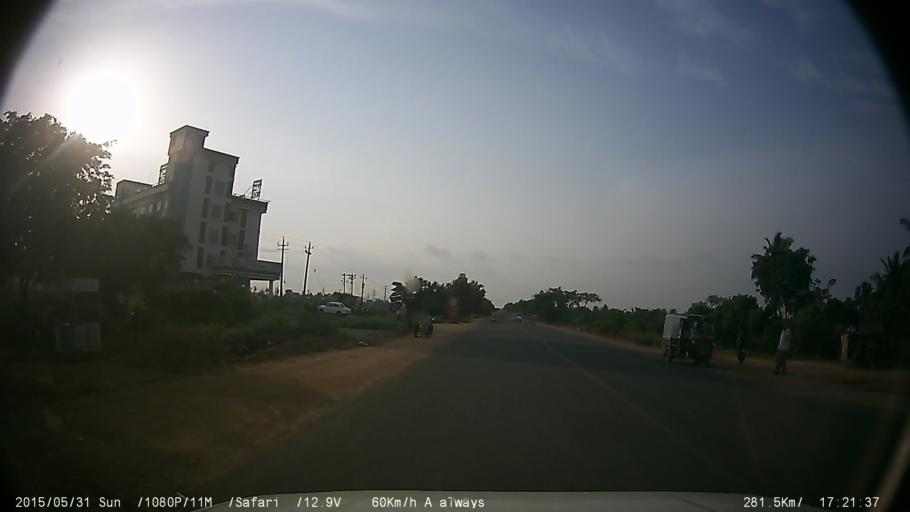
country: IN
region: Karnataka
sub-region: Chamrajnagar
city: Gundlupet
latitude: 11.8290
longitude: 76.6789
